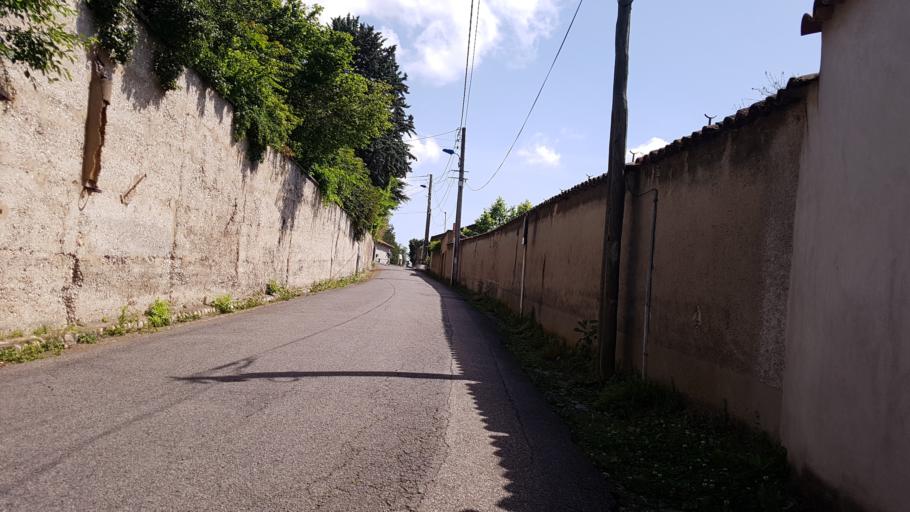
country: FR
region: Rhone-Alpes
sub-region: Departement du Rhone
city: Caluire-et-Cuire
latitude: 45.7893
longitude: 4.8538
